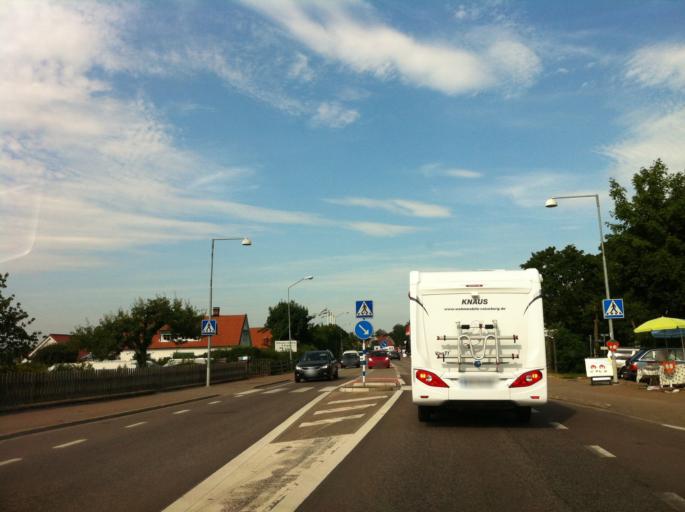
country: SE
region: Kalmar
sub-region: Borgholms Kommun
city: Borgholm
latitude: 56.8793
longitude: 16.7186
